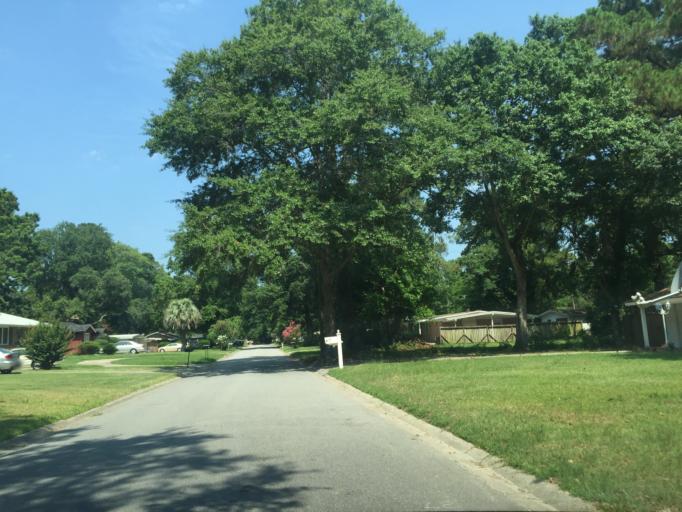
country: US
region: Georgia
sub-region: Chatham County
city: Montgomery
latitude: 31.9745
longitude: -81.1348
